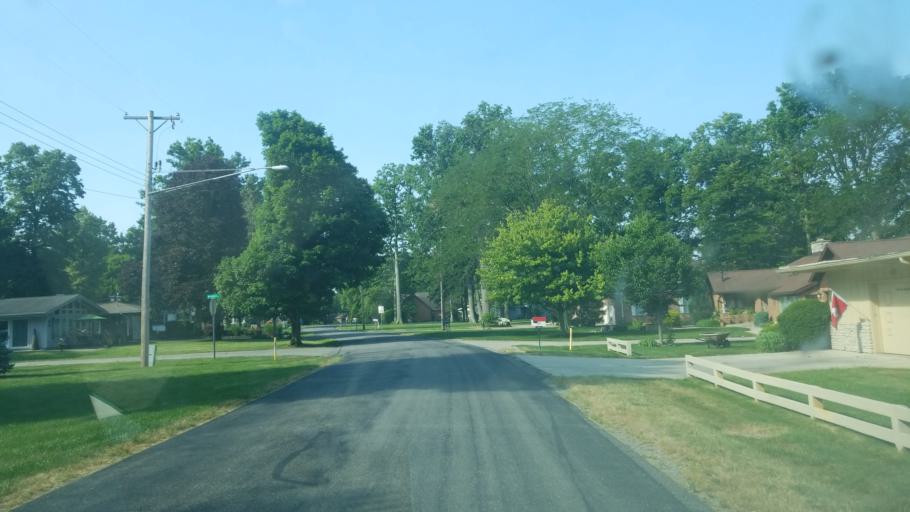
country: US
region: Ohio
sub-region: Logan County
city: Russells Point
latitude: 40.5001
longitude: -83.8734
